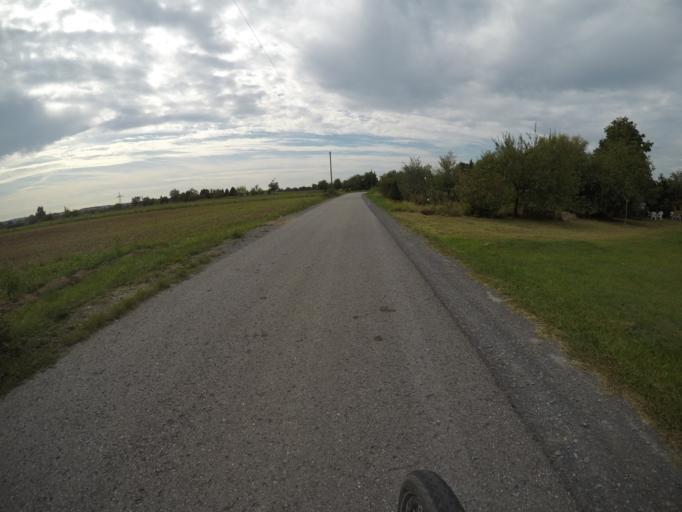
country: DE
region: Baden-Wuerttemberg
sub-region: Karlsruhe Region
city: Sankt Leon-Rot
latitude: 49.2548
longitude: 8.6313
